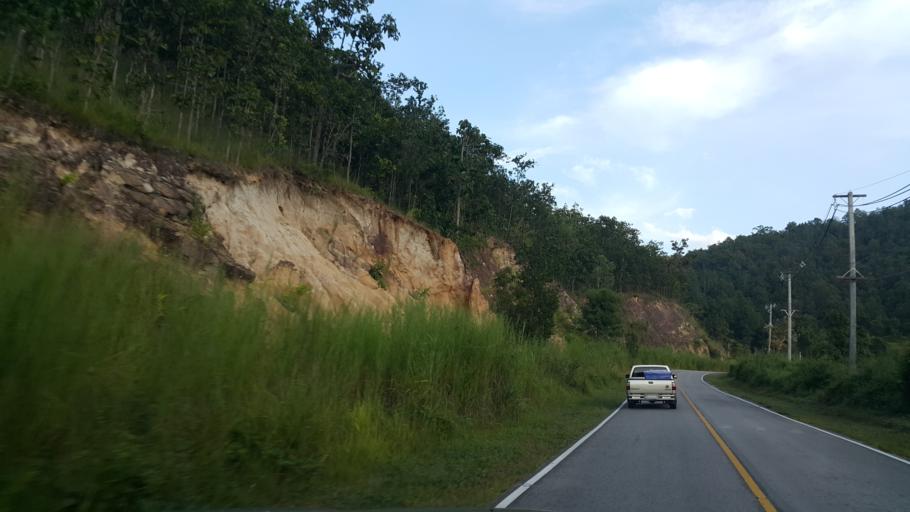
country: TH
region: Chiang Mai
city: Mae On
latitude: 18.7272
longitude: 99.2646
